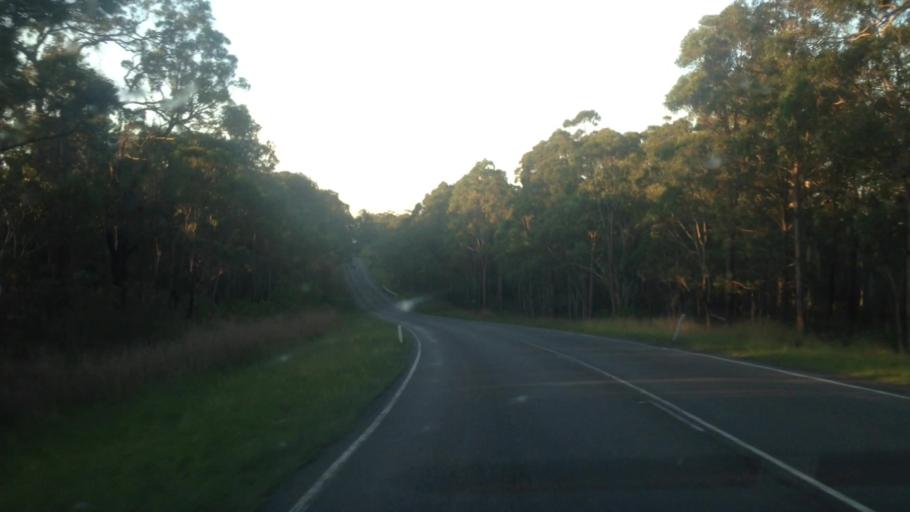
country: AU
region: New South Wales
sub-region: Lake Macquarie Shire
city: Dora Creek
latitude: -33.1479
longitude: 151.4792
